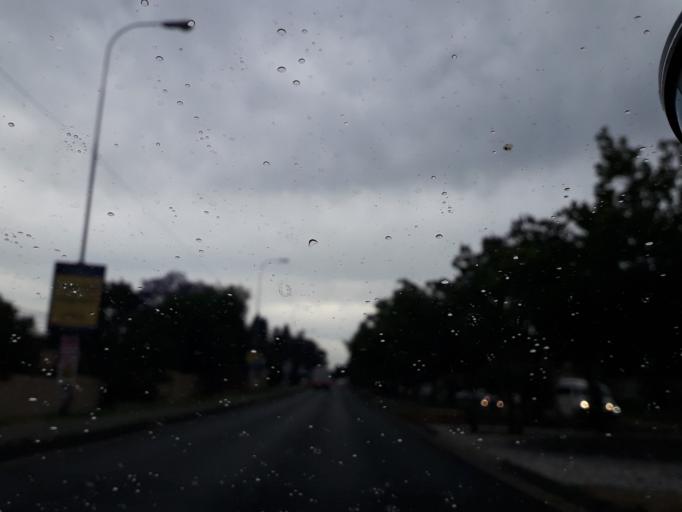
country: ZA
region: Gauteng
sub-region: City of Johannesburg Metropolitan Municipality
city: Johannesburg
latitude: -26.0918
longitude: 28.0225
